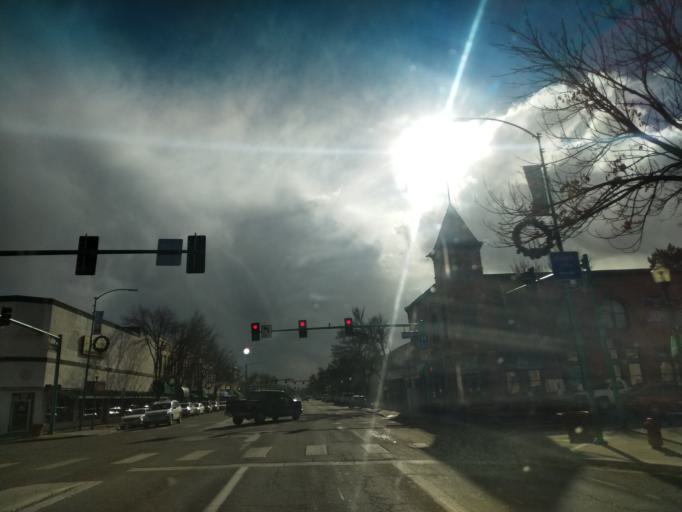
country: US
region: Colorado
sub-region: Delta County
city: Delta
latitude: 38.7433
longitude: -108.0709
